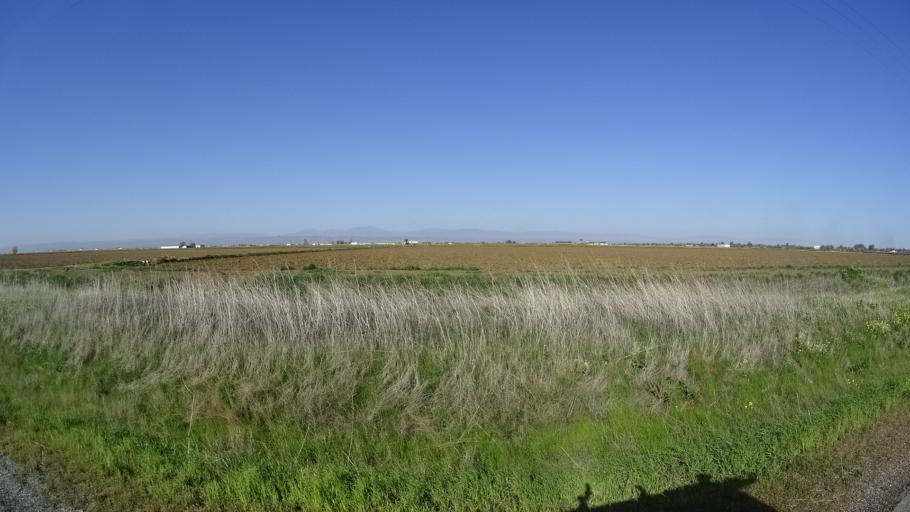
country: US
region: California
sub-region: Glenn County
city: Willows
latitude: 39.4989
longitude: -122.1745
